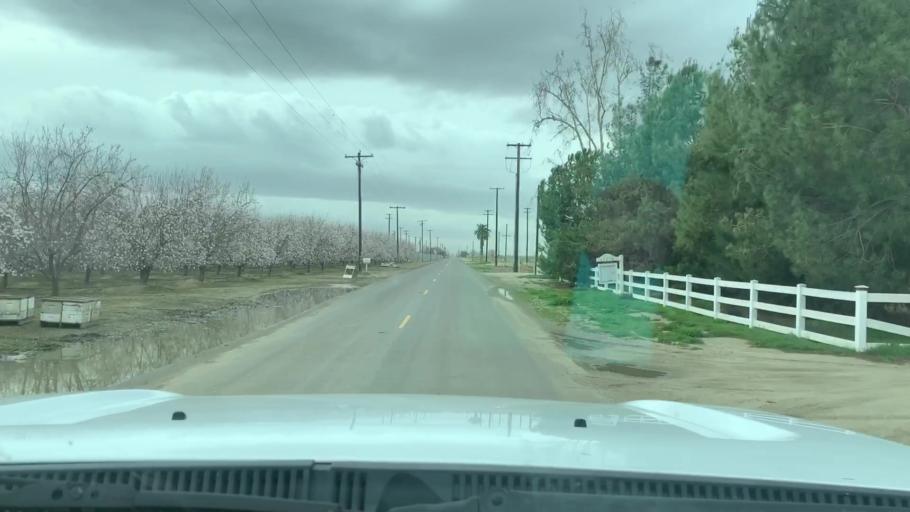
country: US
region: California
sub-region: Kern County
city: Shafter
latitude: 35.5292
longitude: -119.2668
